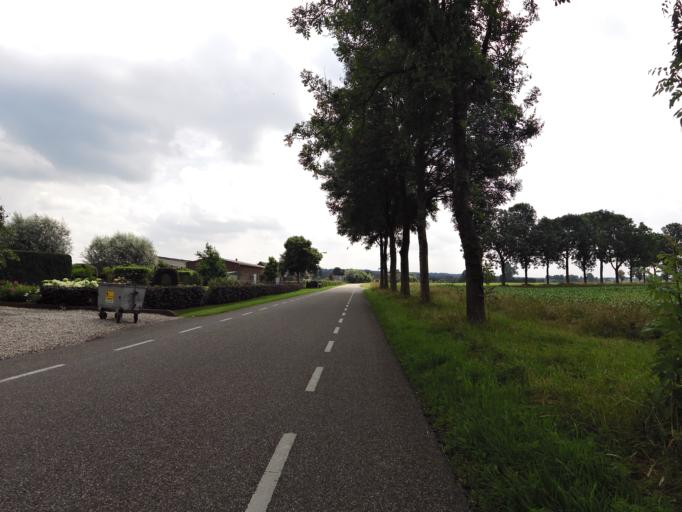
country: NL
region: Gelderland
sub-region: Gemeente Montferland
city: s-Heerenberg
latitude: 51.9323
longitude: 6.2048
